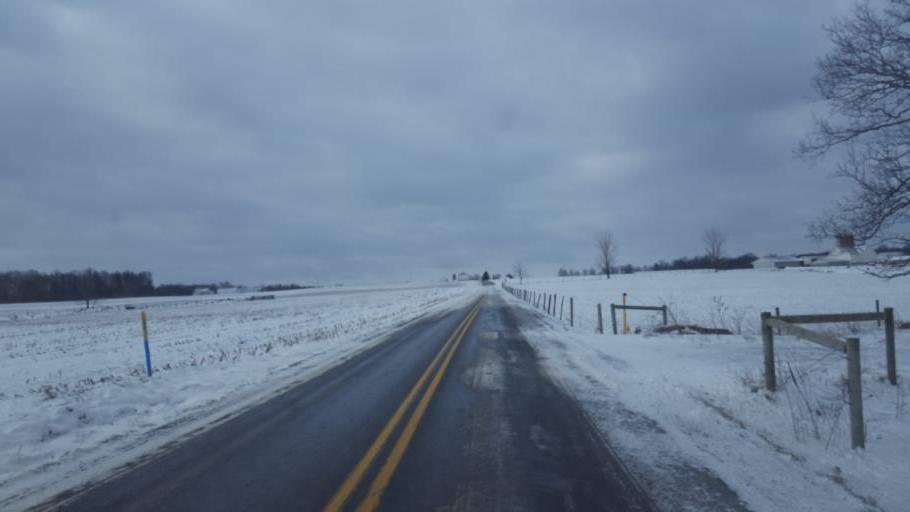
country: US
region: Pennsylvania
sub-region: Lawrence County
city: New Wilmington
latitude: 41.1458
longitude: -80.2709
